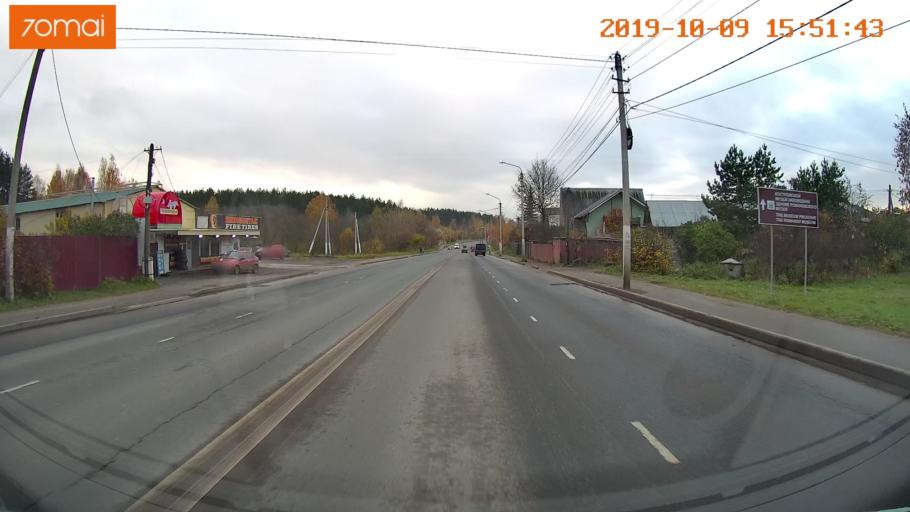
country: RU
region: Kostroma
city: Oktyabr'skiy
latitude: 57.7953
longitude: 40.9763
